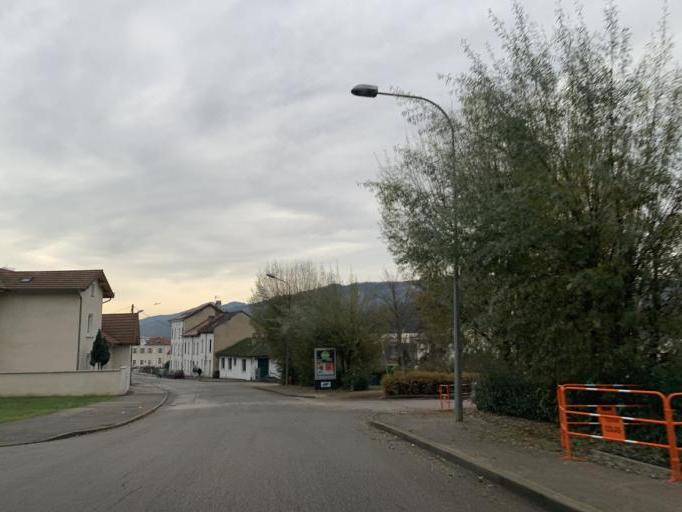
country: FR
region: Rhone-Alpes
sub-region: Departement de l'Ain
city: Belley
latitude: 45.7579
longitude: 5.6942
